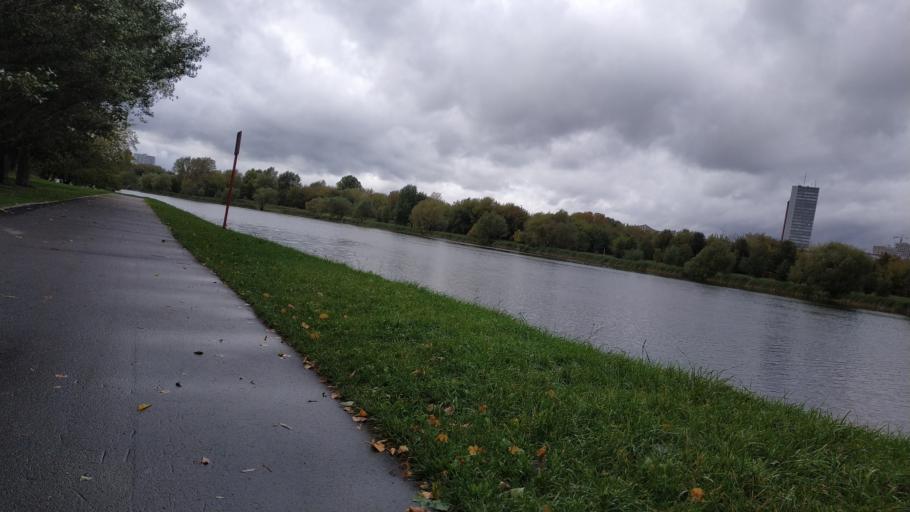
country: RU
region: Moscow
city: Metrogorodok
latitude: 55.7935
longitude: 37.7649
